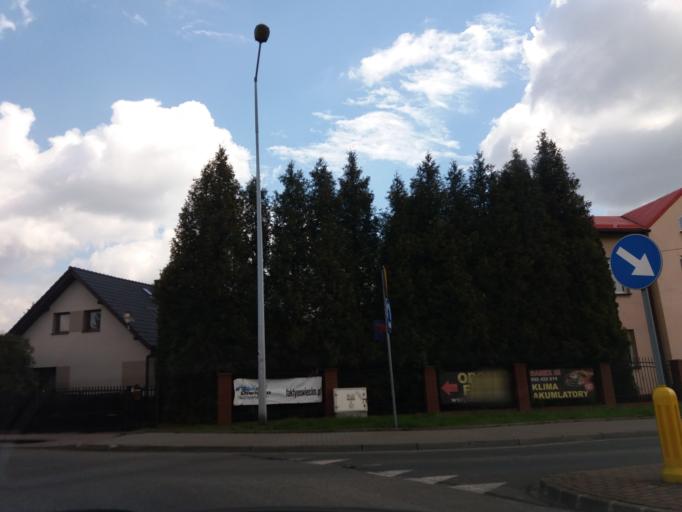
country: PL
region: Lesser Poland Voivodeship
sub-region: Powiat oswiecimski
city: Oswiecim
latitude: 50.0491
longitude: 19.2139
